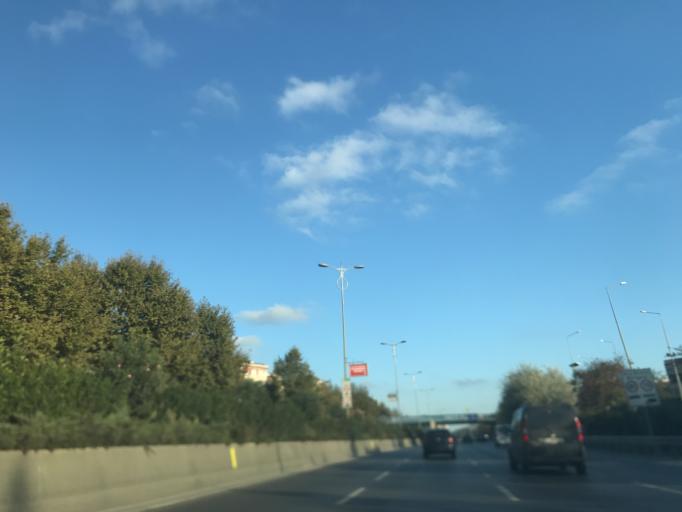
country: TR
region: Istanbul
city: Esenler
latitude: 41.0508
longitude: 28.8720
